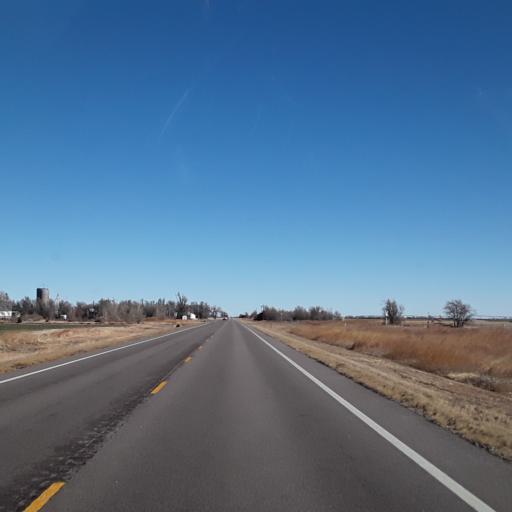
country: US
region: Kansas
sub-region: Pawnee County
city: Larned
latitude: 38.1137
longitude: -99.1883
